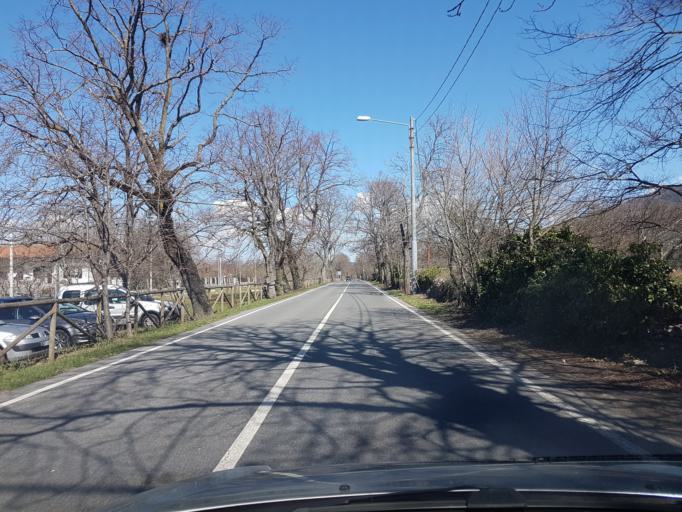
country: IT
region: Friuli Venezia Giulia
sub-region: Provincia di Trieste
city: Dolina
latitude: 45.6434
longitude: 13.8676
